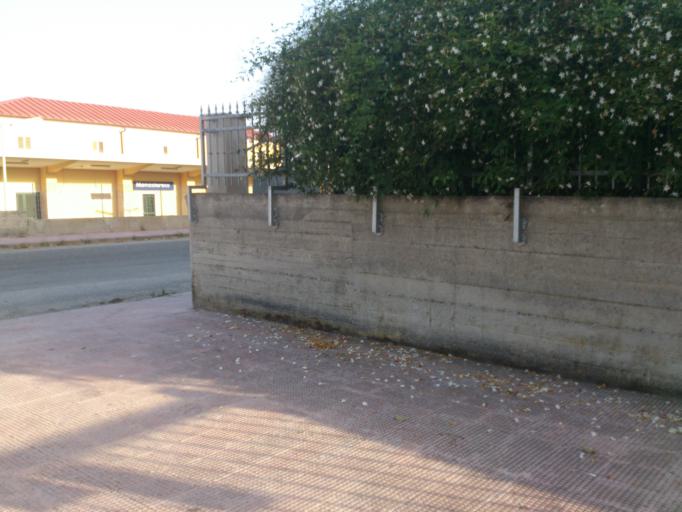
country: IT
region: Calabria
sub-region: Provincia di Reggio Calabria
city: Monasterace Marina
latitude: 38.4379
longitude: 16.5742
